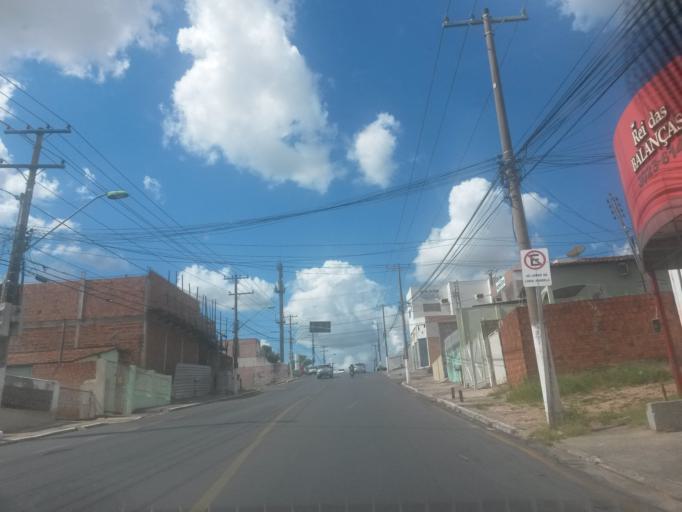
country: BR
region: Mato Grosso
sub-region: Cuiaba
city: Cuiaba
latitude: -15.5981
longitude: -56.0847
